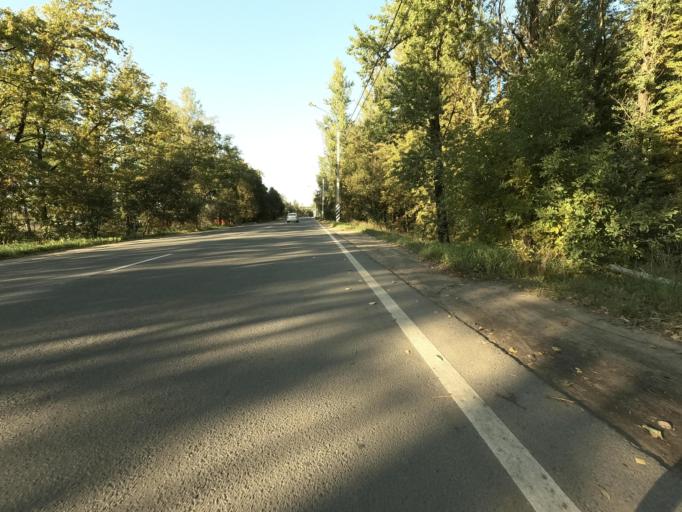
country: RU
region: St.-Petersburg
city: Kolpino
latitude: 59.7510
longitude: 30.6159
